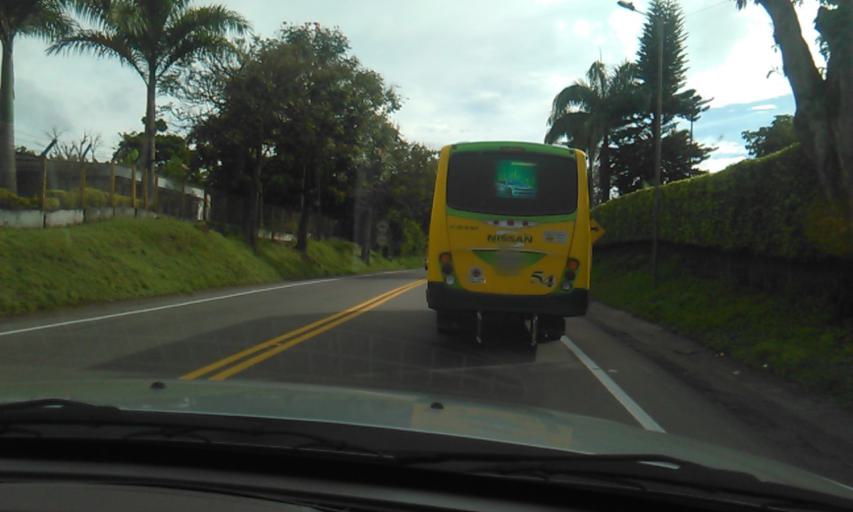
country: CO
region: Quindio
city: Armenia
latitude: 4.4833
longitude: -75.7000
